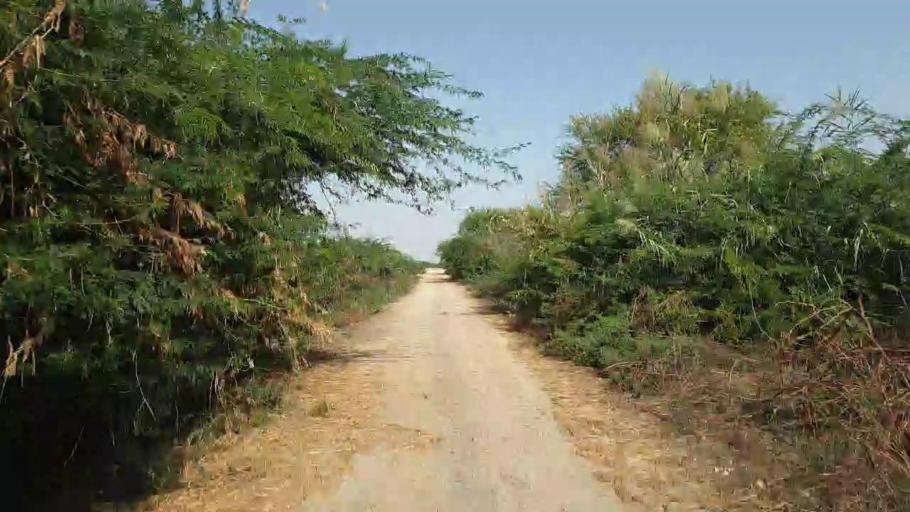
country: PK
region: Sindh
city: Tando Bago
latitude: 24.7253
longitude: 69.0735
